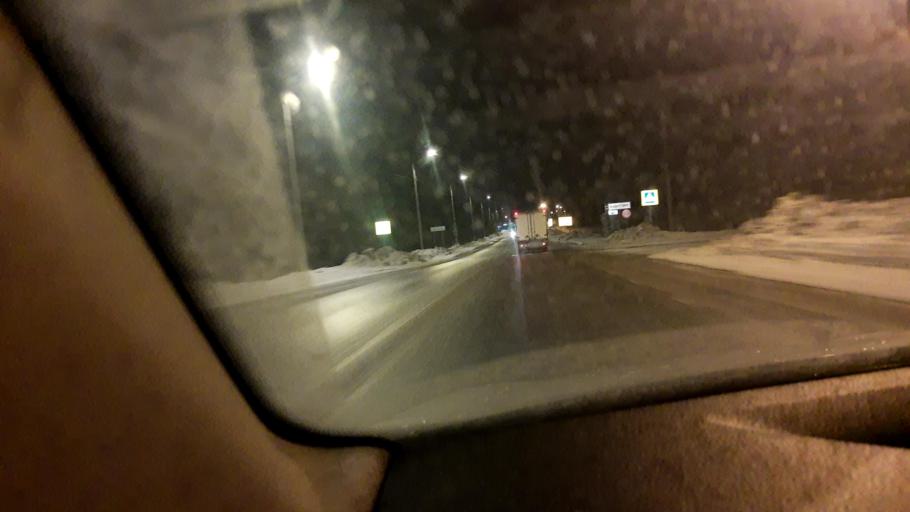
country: RU
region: Moskovskaya
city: Skoropuskovskiy
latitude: 56.3784
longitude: 38.1075
